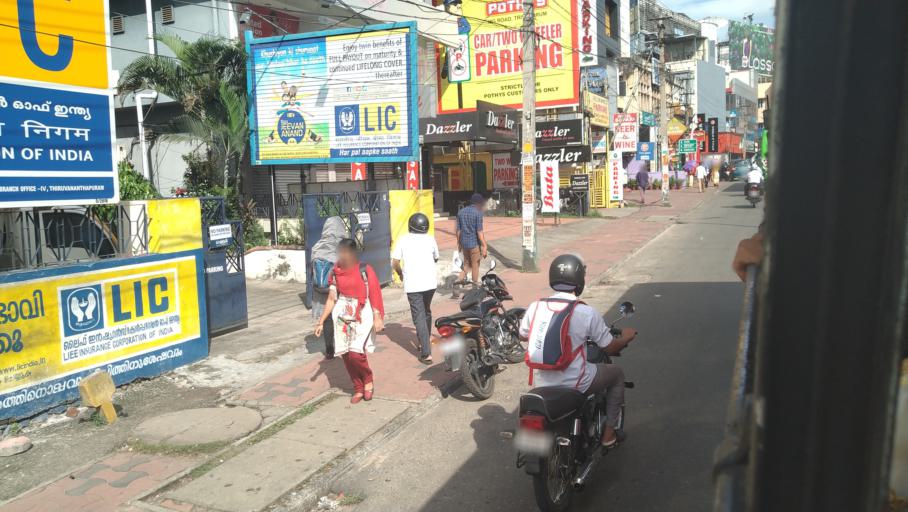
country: IN
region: Kerala
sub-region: Thiruvananthapuram
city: Thiruvananthapuram
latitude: 8.4888
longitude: 76.9473
